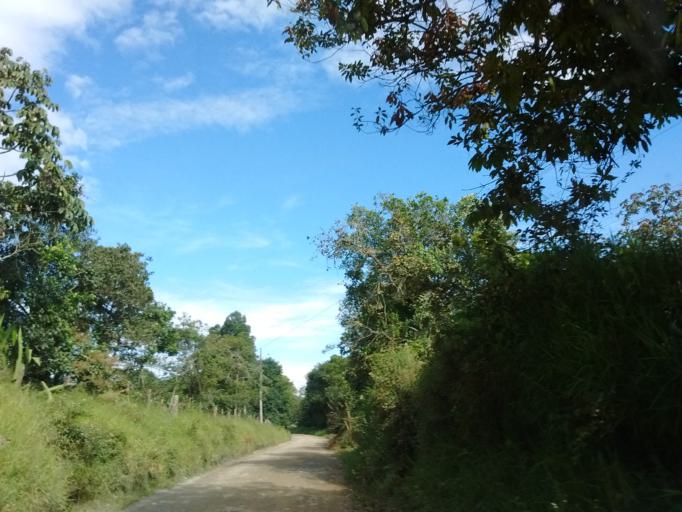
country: CO
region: Cauca
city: Cajibio
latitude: 2.6197
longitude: -76.5864
